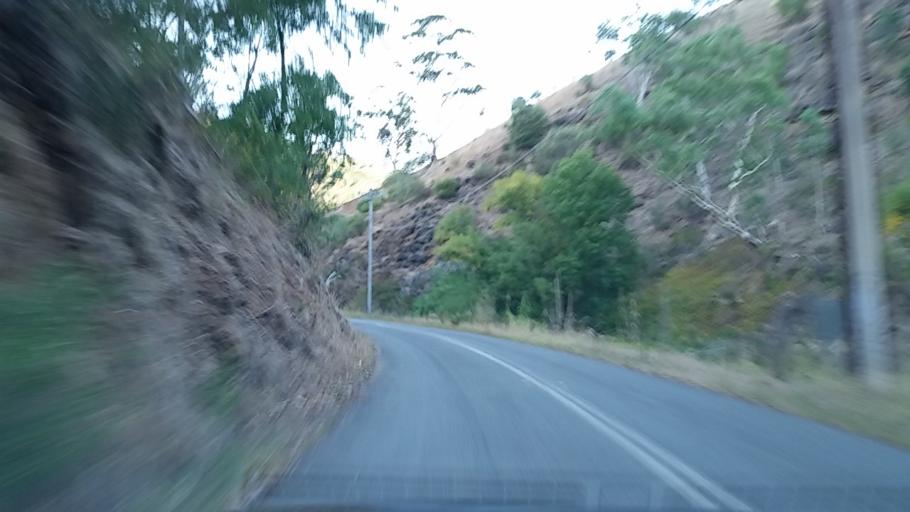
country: AU
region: South Australia
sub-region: Campbelltown
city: Athelstone
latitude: -34.8709
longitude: 138.7524
